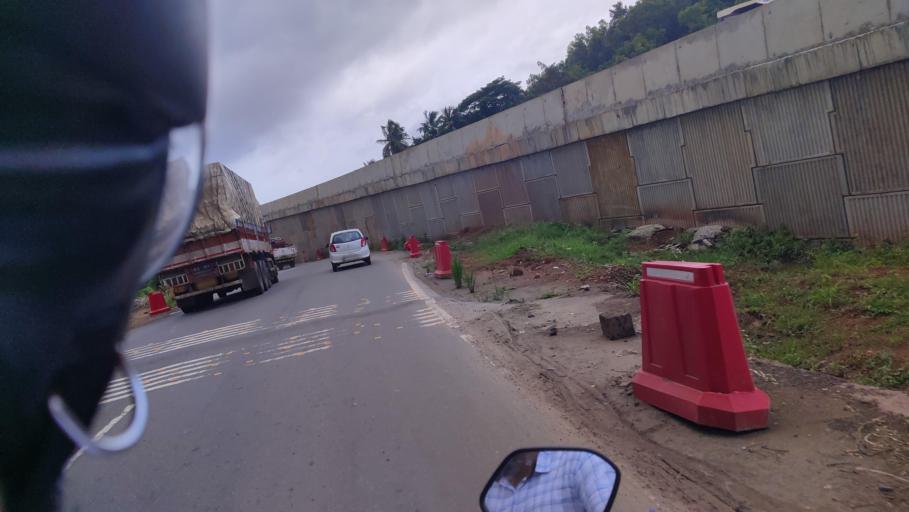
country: IN
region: Kerala
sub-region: Kasaragod District
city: Nileshwar
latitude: 12.2415
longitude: 75.1486
